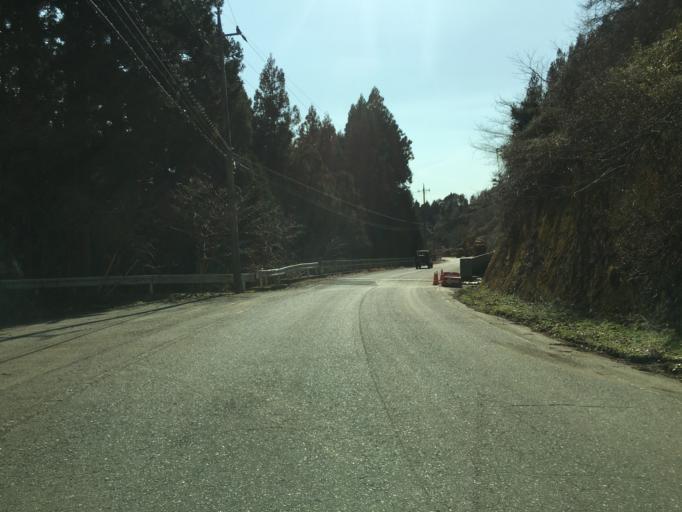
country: JP
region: Ibaraki
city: Takahagi
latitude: 36.8115
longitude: 140.5815
